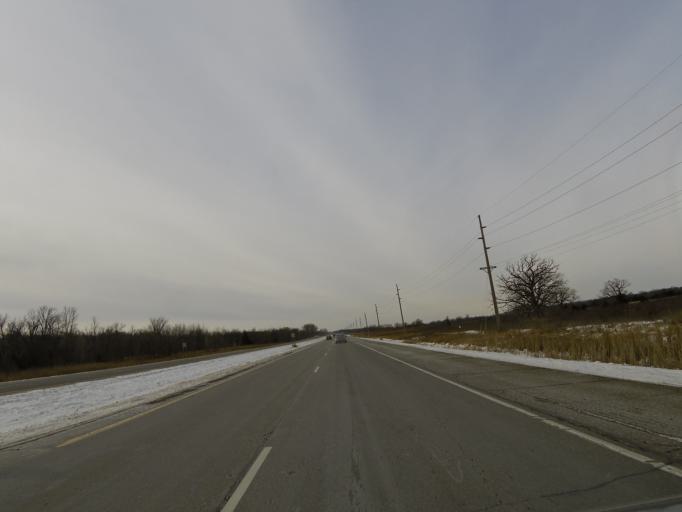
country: US
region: Minnesota
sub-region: Scott County
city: Jordan
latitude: 44.6533
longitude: -93.6858
